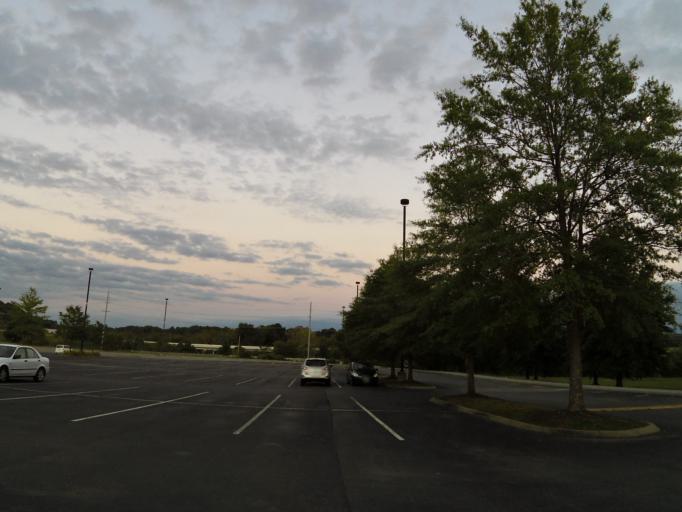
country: US
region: Tennessee
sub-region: Blount County
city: Eagleton Village
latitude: 35.8099
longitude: -83.9479
